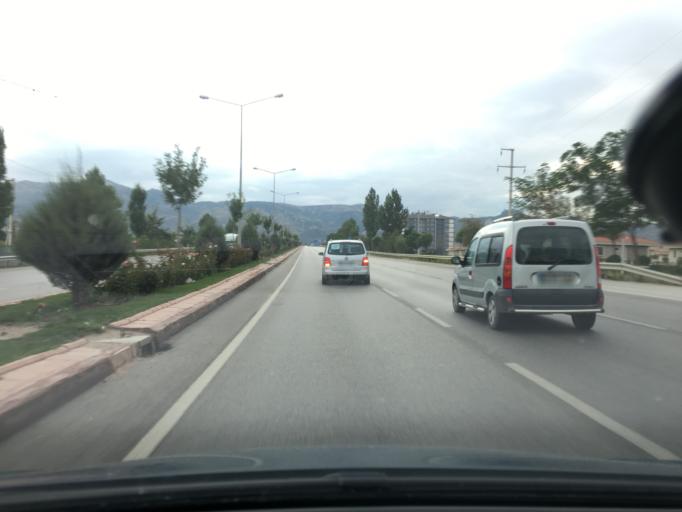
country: TR
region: Afyonkarahisar
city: Afyonkarahisar
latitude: 38.7837
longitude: 30.4993
